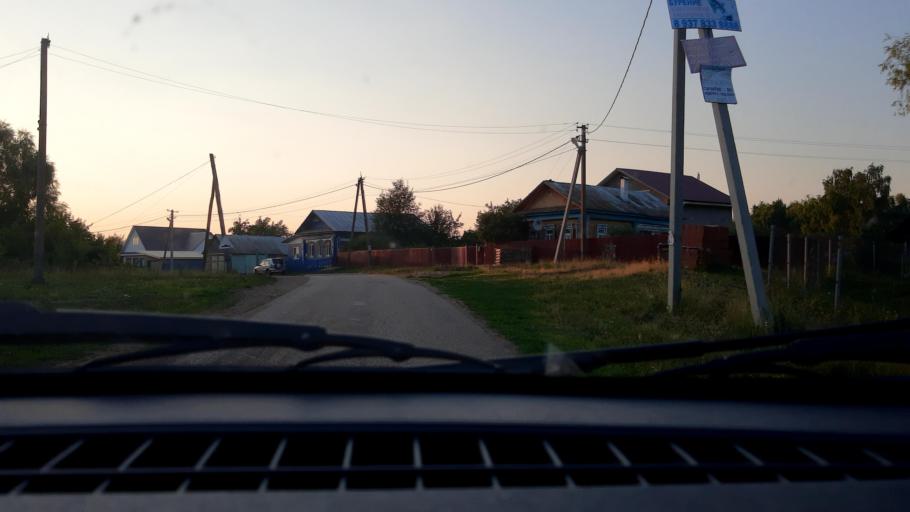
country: RU
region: Bashkortostan
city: Blagoveshchensk
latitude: 54.9425
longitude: 55.8805
